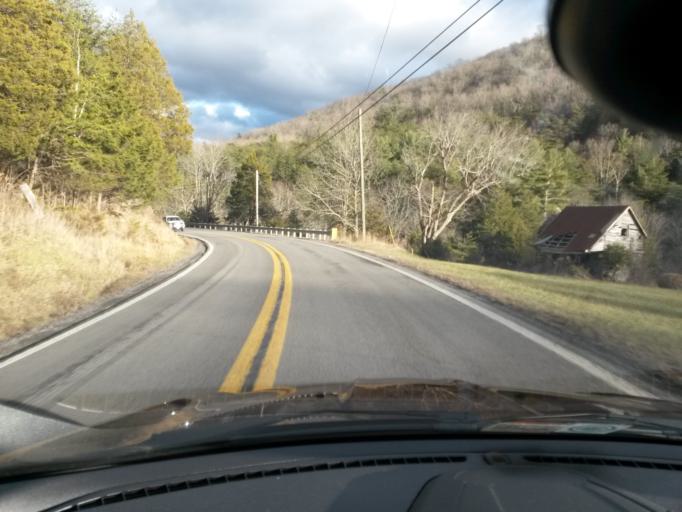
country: US
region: West Virginia
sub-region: Monroe County
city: Union
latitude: 37.5246
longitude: -80.6133
